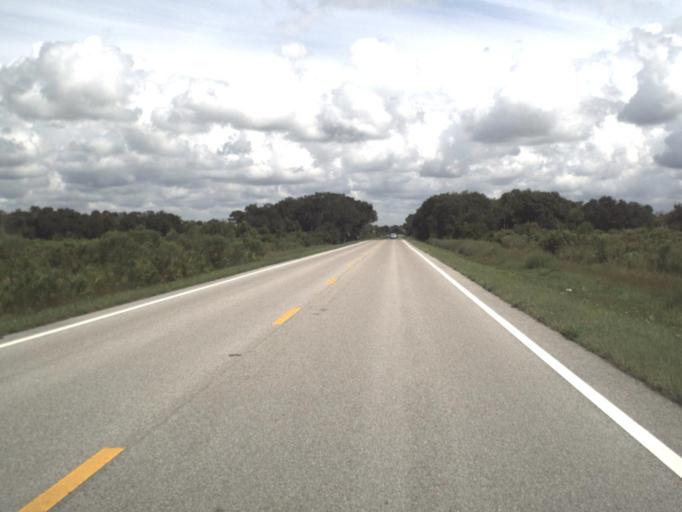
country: US
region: Florida
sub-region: Sarasota County
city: Warm Mineral Springs
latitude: 27.2176
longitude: -82.2763
